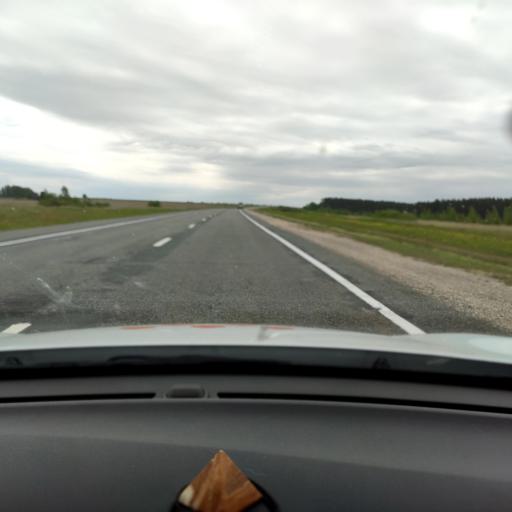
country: RU
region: Tatarstan
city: Laishevo
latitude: 55.5067
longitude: 49.8242
